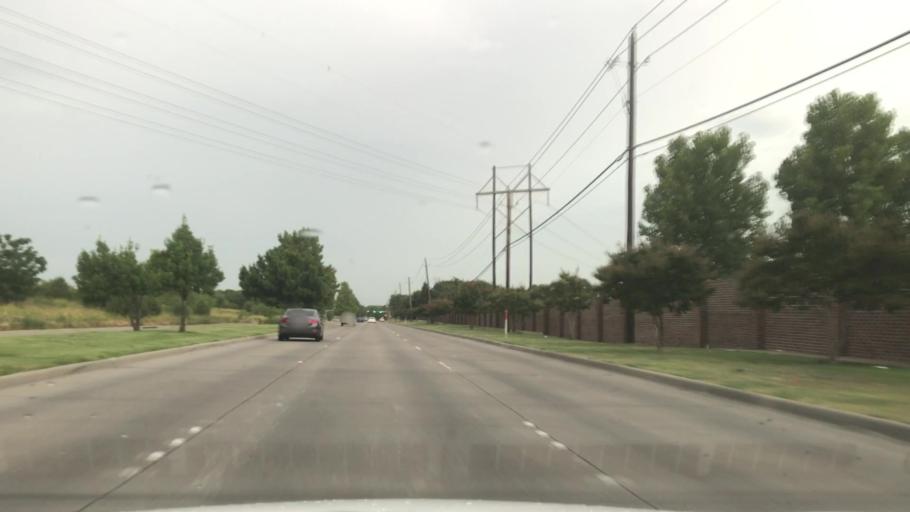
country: US
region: Texas
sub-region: Dallas County
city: Mesquite
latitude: 32.7418
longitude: -96.5767
